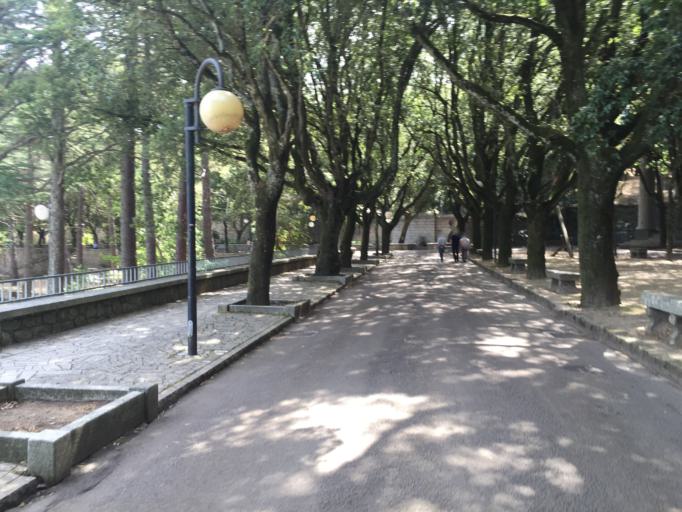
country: IT
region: Sardinia
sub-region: Provincia di Olbia-Tempio
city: Tempio Pausania
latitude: 40.8996
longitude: 9.0989
